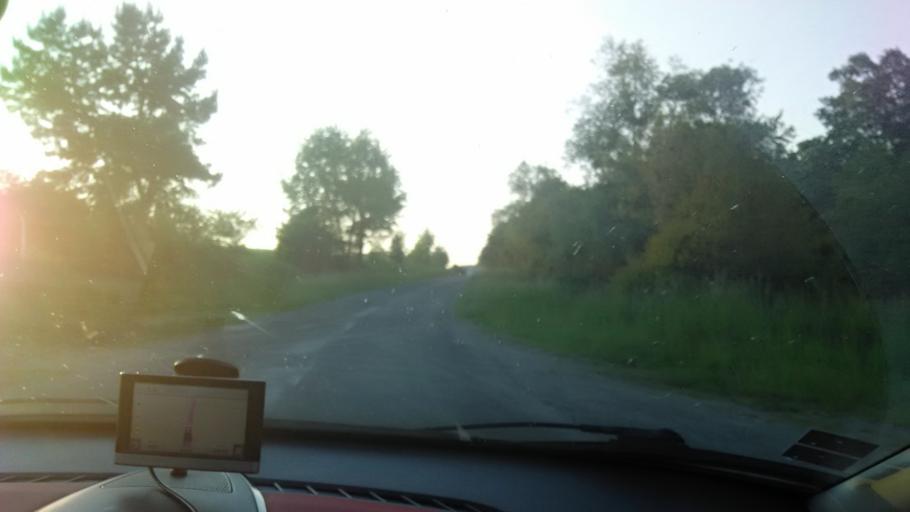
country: SK
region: Presovsky
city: Sabinov
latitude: 49.0088
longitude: 21.0751
